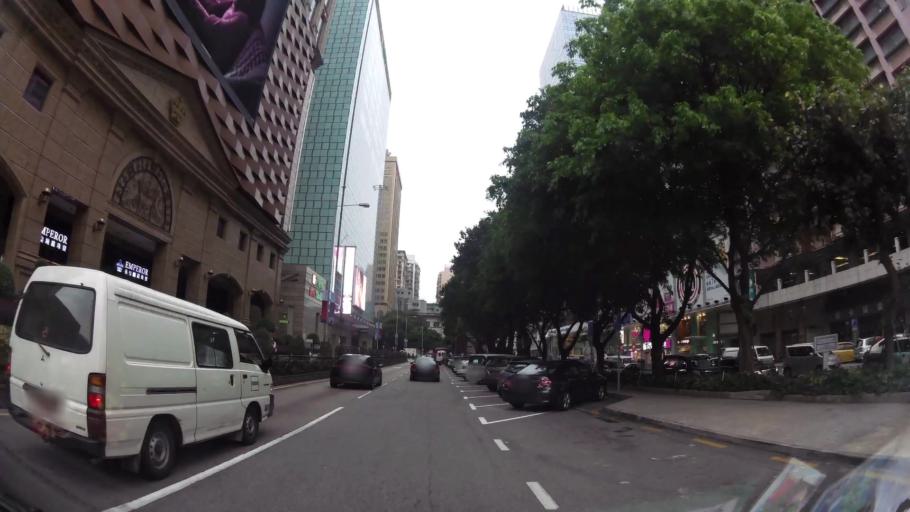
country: MO
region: Macau
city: Macau
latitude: 22.1907
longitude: 113.5413
